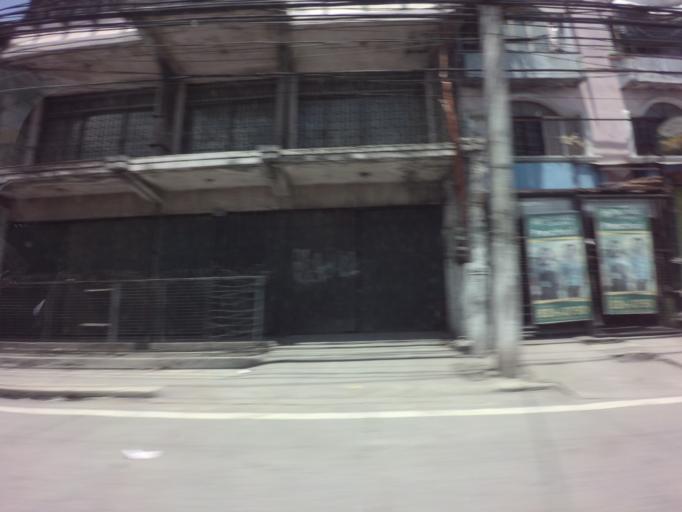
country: PH
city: Sambayanihan People's Village
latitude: 14.4908
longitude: 120.9874
